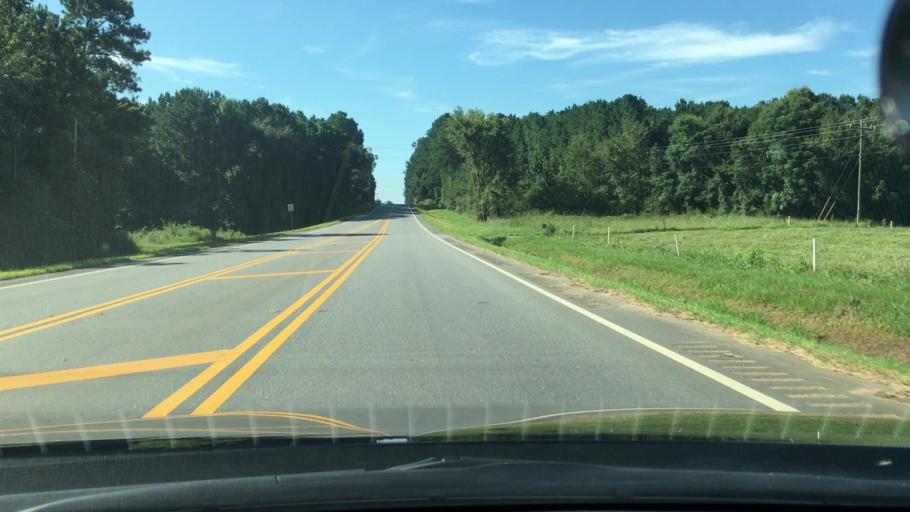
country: US
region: Georgia
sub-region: Putnam County
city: Jefferson
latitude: 33.4643
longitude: -83.4143
